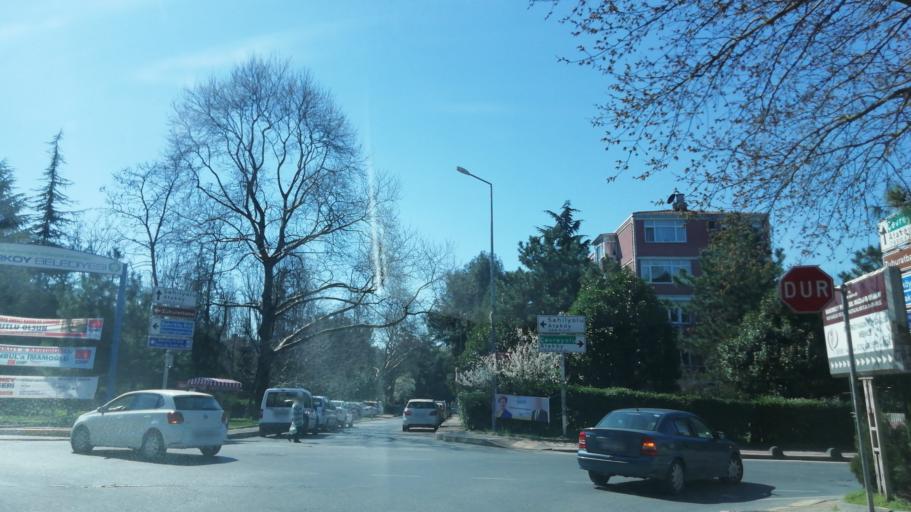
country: TR
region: Istanbul
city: Bahcelievler
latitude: 40.9832
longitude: 28.8651
